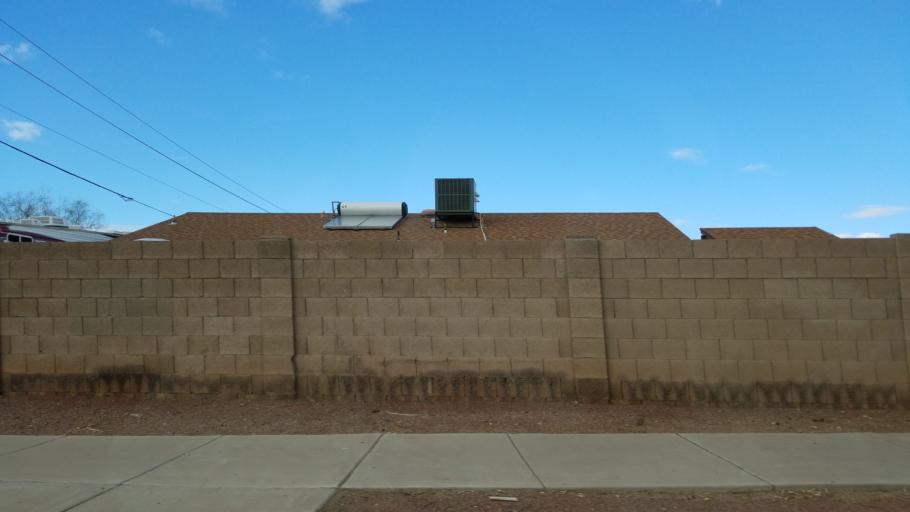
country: US
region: Arizona
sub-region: Maricopa County
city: Glendale
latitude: 33.6547
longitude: -112.0911
